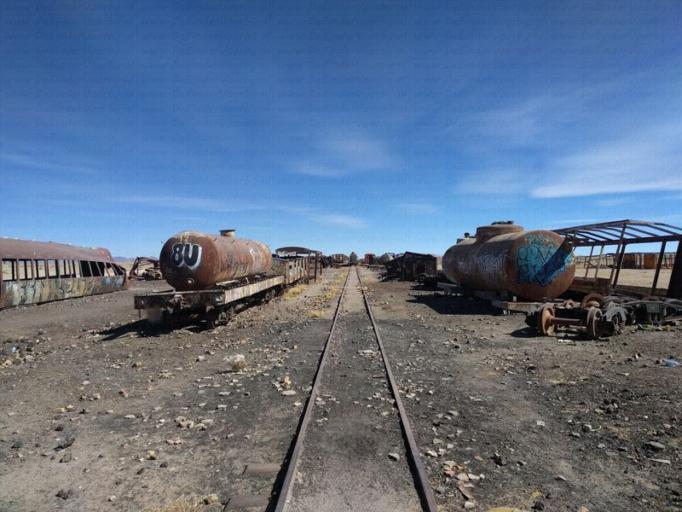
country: BO
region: Potosi
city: Uyuni
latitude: -20.4795
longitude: -66.8343
